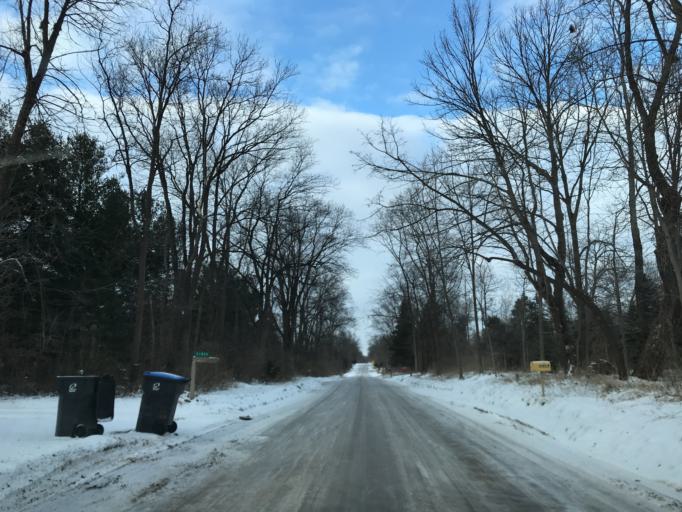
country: US
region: Michigan
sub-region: Oakland County
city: South Lyon
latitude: 42.4435
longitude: -83.5914
